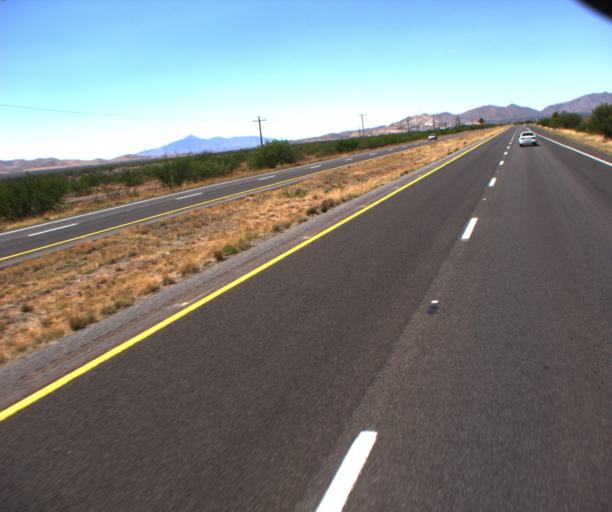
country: US
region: Arizona
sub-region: Cochise County
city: Pirtleville
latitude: 31.3640
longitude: -109.6938
